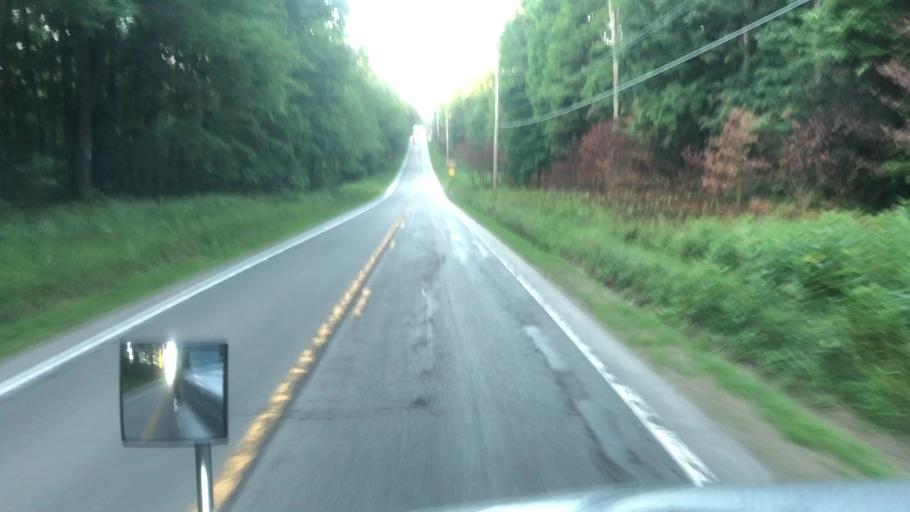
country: US
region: Pennsylvania
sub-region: Venango County
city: Hasson Heights
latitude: 41.5206
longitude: -79.6174
